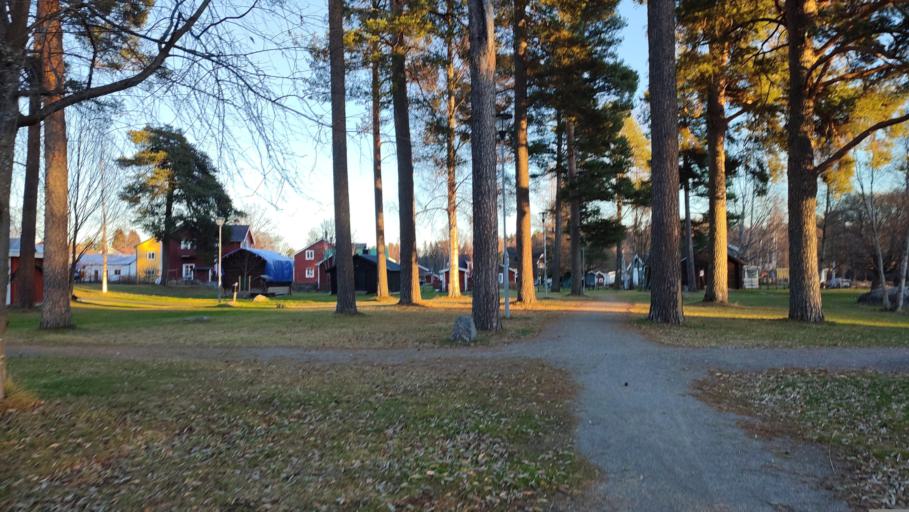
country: SE
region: Vaesterbotten
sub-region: Skelleftea Kommun
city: Burea
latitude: 64.6192
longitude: 21.2040
